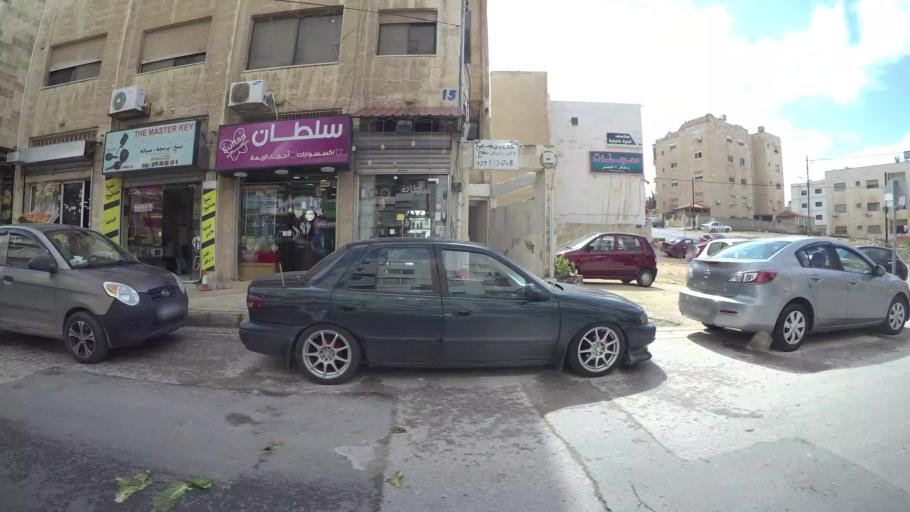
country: JO
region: Amman
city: Al Jubayhah
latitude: 31.9904
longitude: 35.8477
